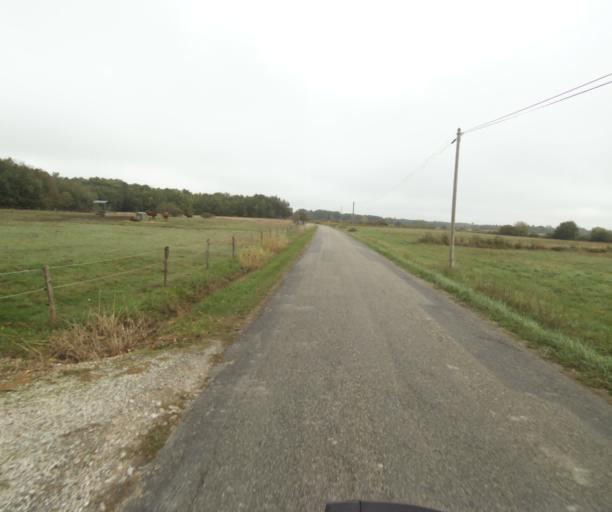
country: FR
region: Midi-Pyrenees
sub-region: Departement du Tarn-et-Garonne
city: Orgueil
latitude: 43.8938
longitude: 1.3879
